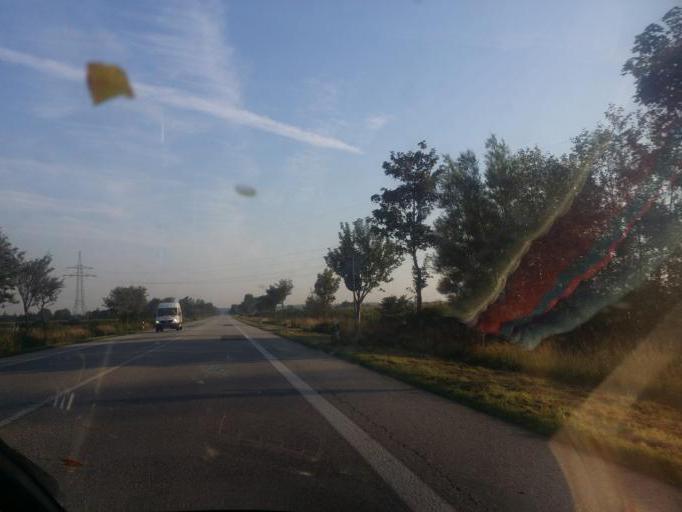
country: DE
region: Schleswig-Holstein
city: Bargum
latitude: 54.7043
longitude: 8.9568
